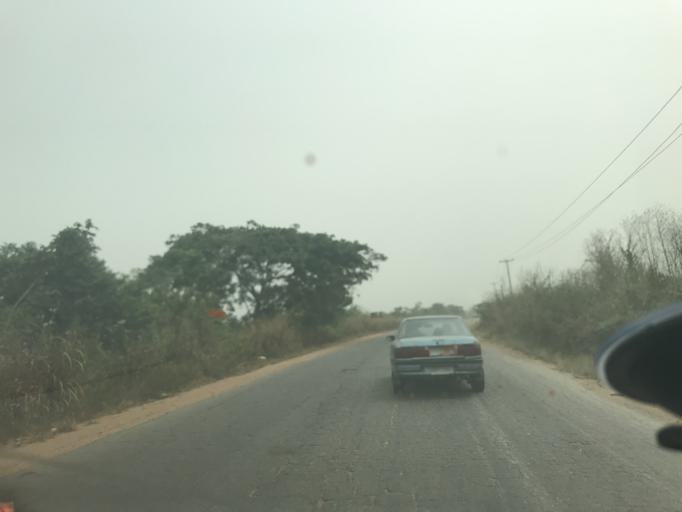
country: NG
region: Ogun
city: Itori
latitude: 6.8911
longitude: 3.1714
